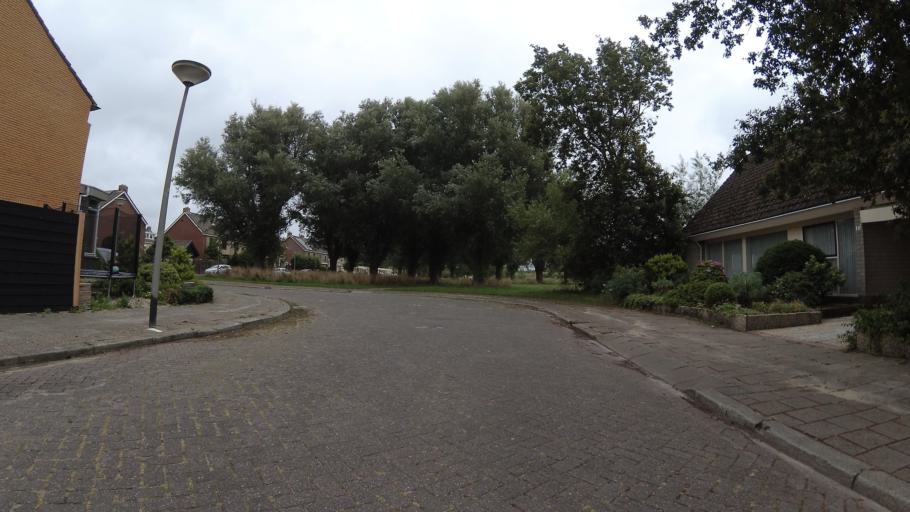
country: NL
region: North Holland
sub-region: Gemeente Den Helder
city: Den Helder
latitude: 52.9302
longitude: 4.7740
